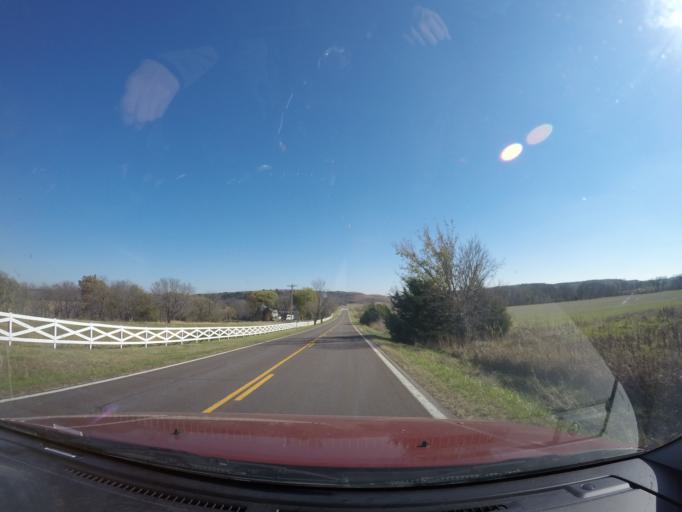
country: US
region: Kansas
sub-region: Geary County
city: Grandview Plaza
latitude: 39.0080
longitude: -96.7437
